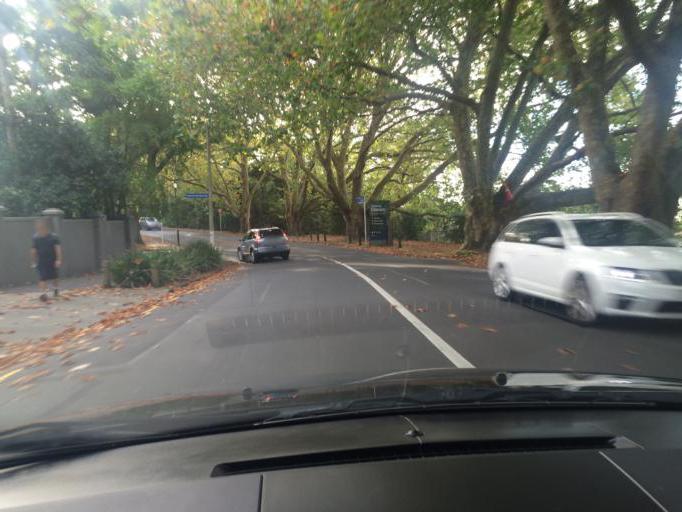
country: NZ
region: Auckland
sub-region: Auckland
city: Auckland
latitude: -36.8615
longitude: 174.7809
